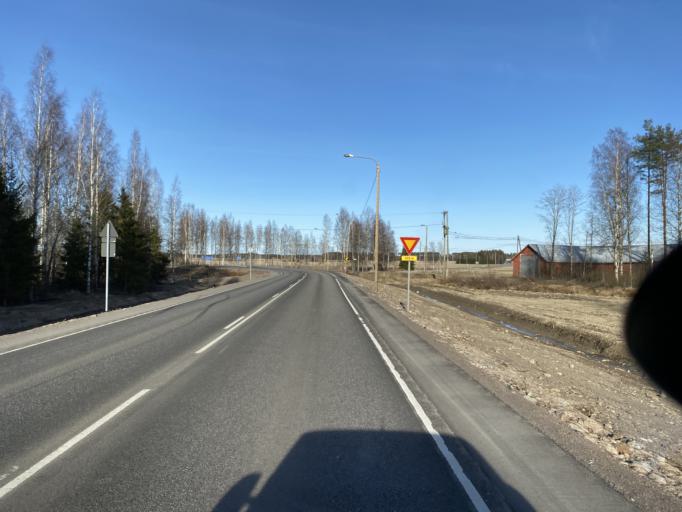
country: FI
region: Satakunta
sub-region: Pori
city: Huittinen
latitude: 61.1769
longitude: 22.5769
